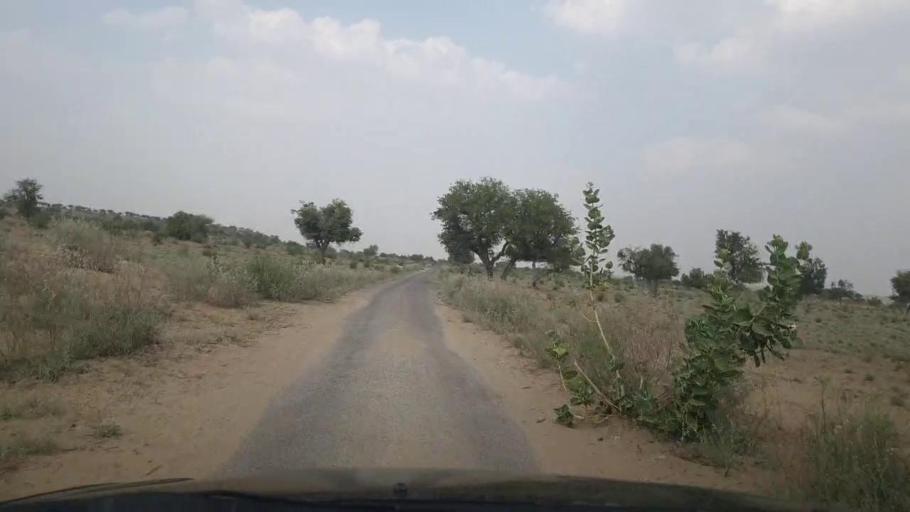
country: PK
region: Sindh
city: Islamkot
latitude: 24.9123
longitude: 70.5610
